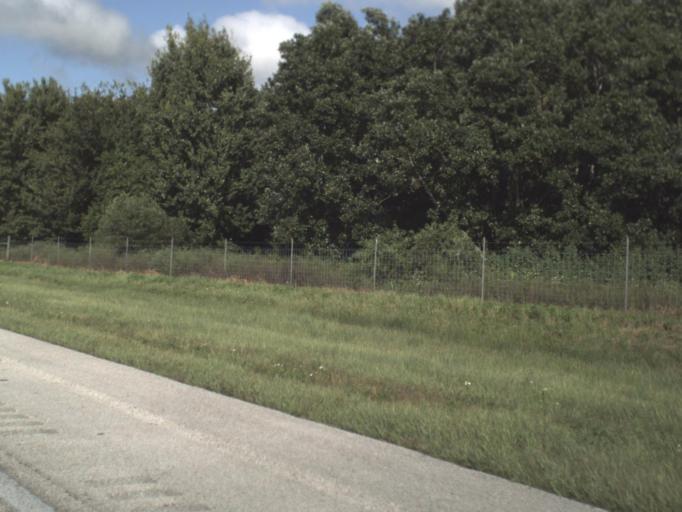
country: US
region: Florida
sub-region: Polk County
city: Polk City
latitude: 28.1592
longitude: -81.7896
